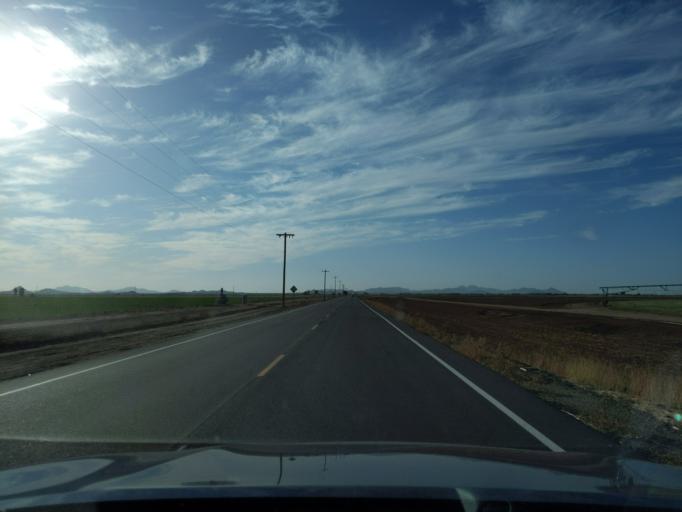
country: US
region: Arizona
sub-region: Pinal County
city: Florence
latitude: 33.1183
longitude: -111.4093
